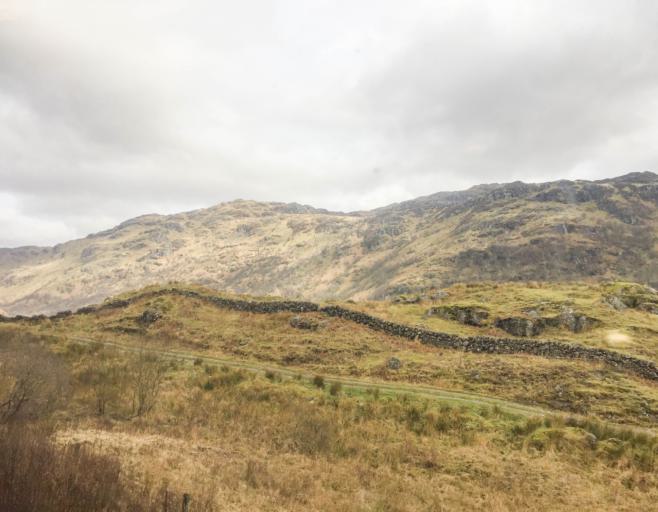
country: GB
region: Scotland
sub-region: Argyll and Bute
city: Garelochhead
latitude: 56.2668
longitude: -4.7059
